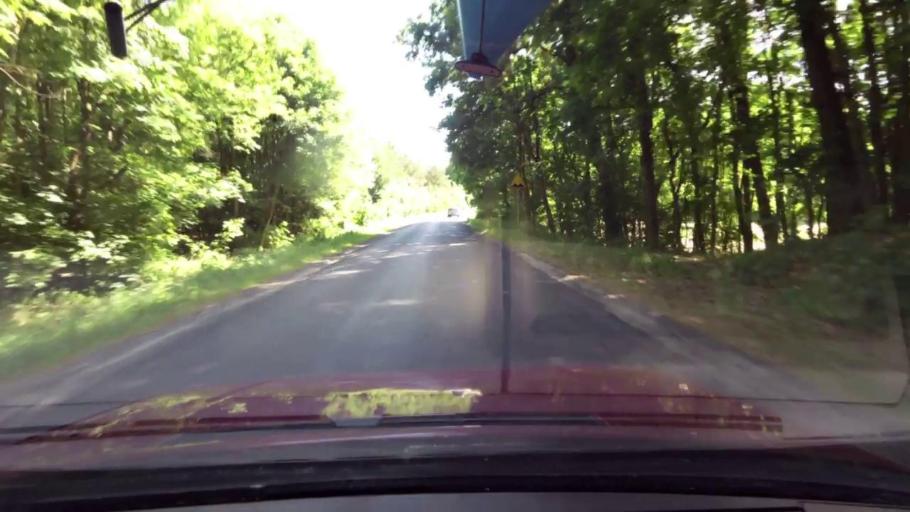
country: PL
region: Pomeranian Voivodeship
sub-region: Powiat slupski
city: Kepice
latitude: 54.2898
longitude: 16.9606
